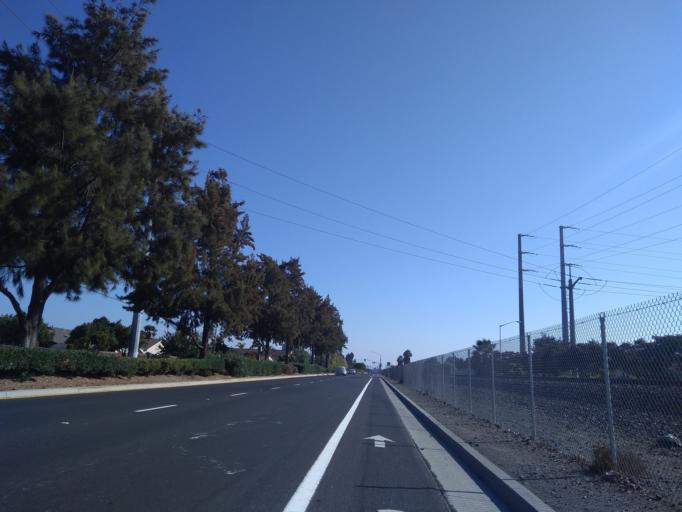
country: US
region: California
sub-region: Santa Clara County
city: Santa Clara
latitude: 37.4030
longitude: -121.9643
